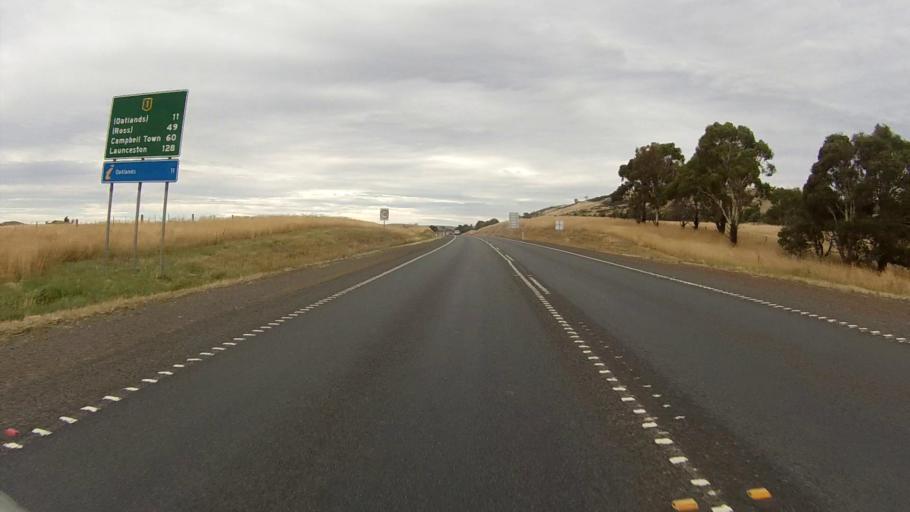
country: AU
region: Tasmania
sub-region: Brighton
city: Bridgewater
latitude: -42.3829
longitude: 147.3167
